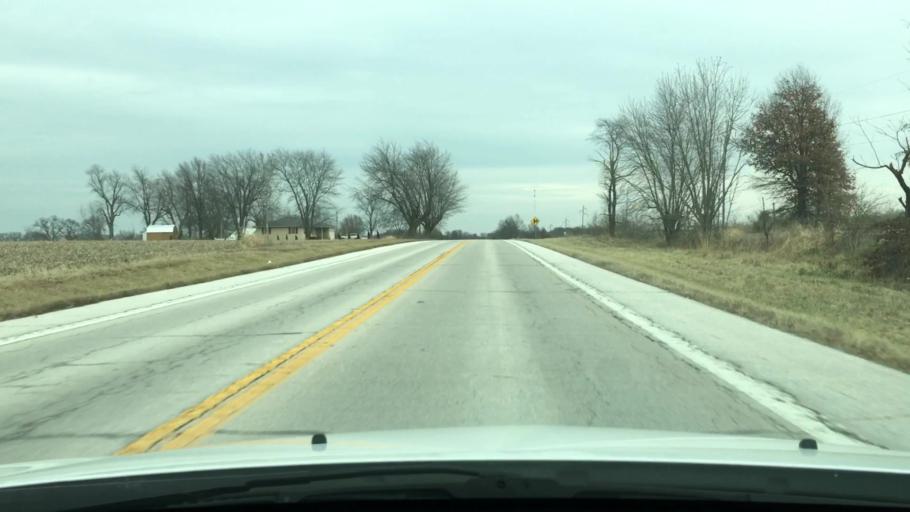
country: US
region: Missouri
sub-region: Audrain County
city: Vandalia
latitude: 39.3318
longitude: -91.4354
